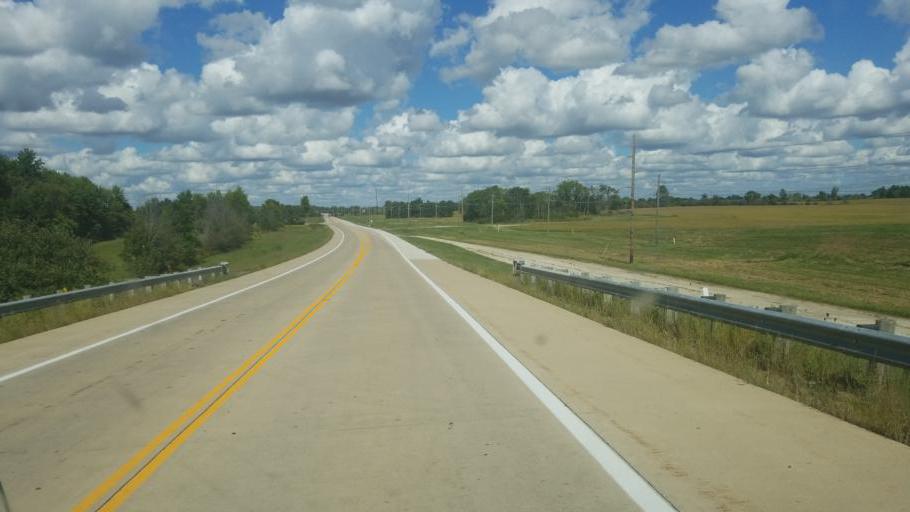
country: US
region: Ohio
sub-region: Champaign County
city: North Lewisburg
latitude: 40.2907
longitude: -83.5207
